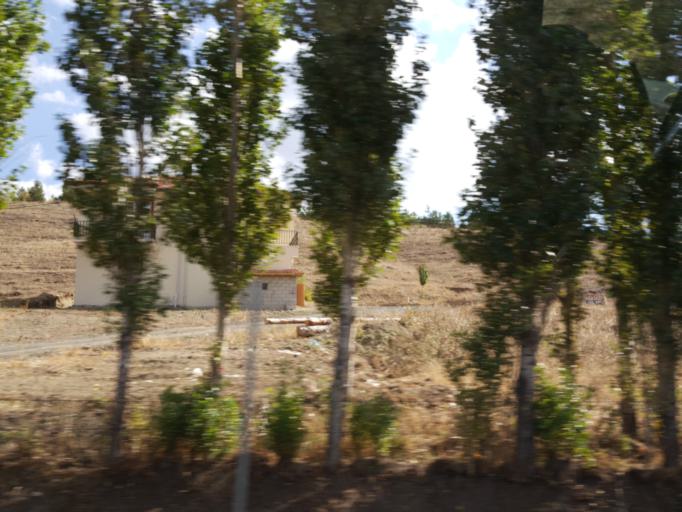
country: TR
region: Tokat
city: Sulusaray
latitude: 39.9891
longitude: 35.9961
